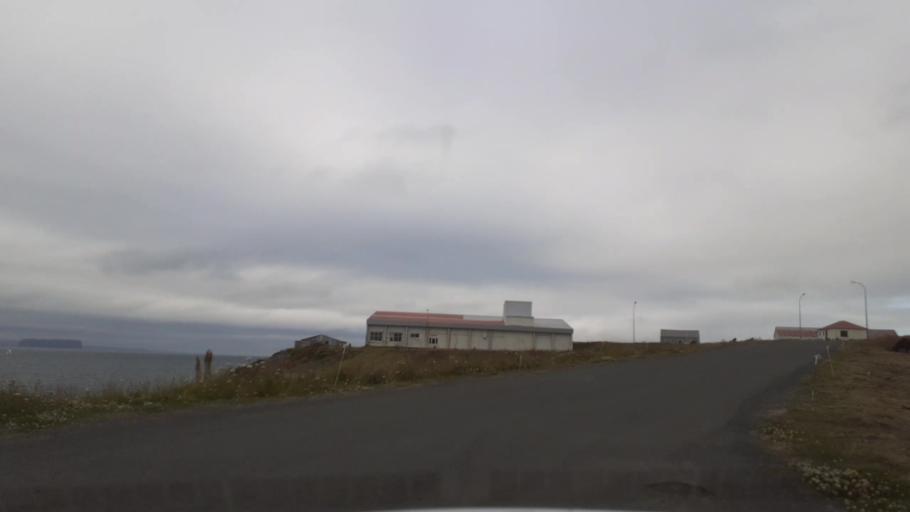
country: IS
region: Northwest
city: Saudarkrokur
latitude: 65.8988
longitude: -19.4232
